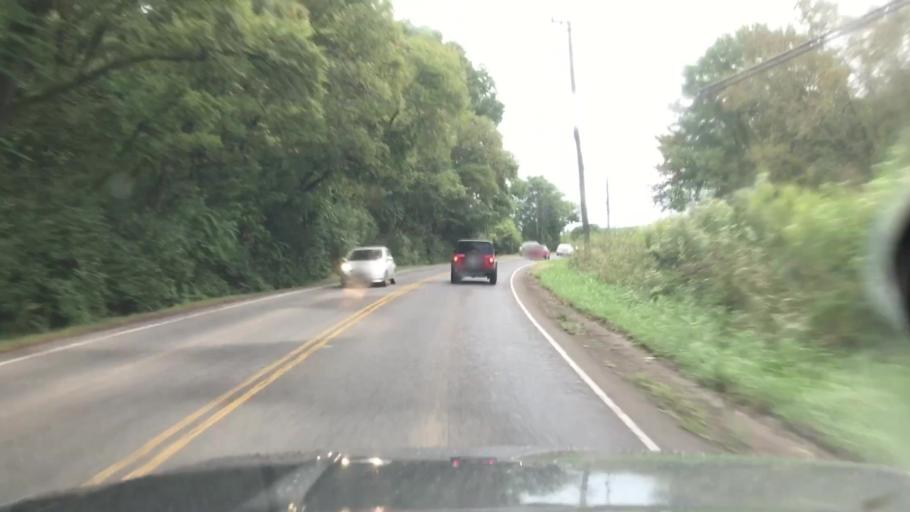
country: US
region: Tennessee
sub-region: Davidson County
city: Lakewood
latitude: 36.1792
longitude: -86.6187
